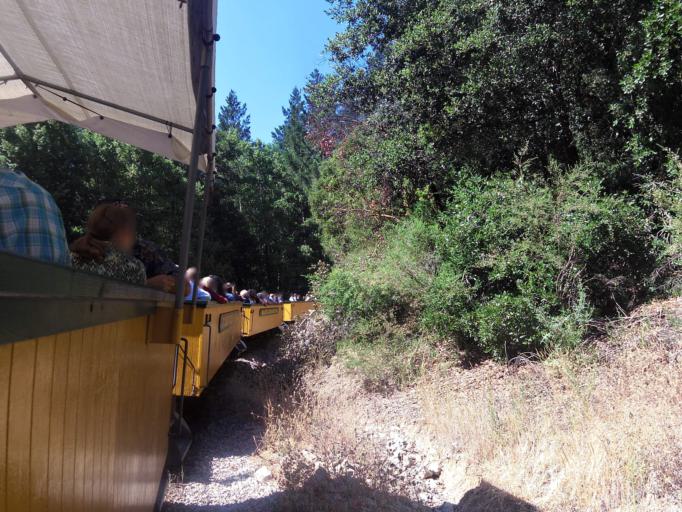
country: US
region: California
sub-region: Santa Cruz County
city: Mount Hermon
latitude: 37.0409
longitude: -122.0589
